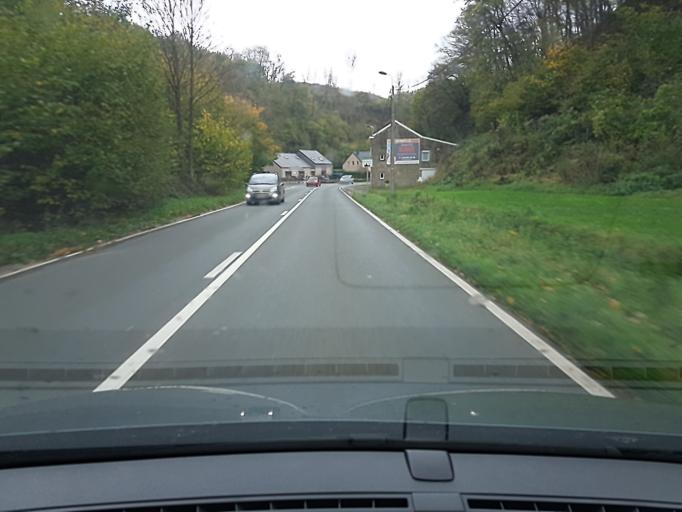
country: BE
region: Wallonia
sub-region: Province de Liege
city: Aywaille
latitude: 50.4868
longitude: 5.7196
